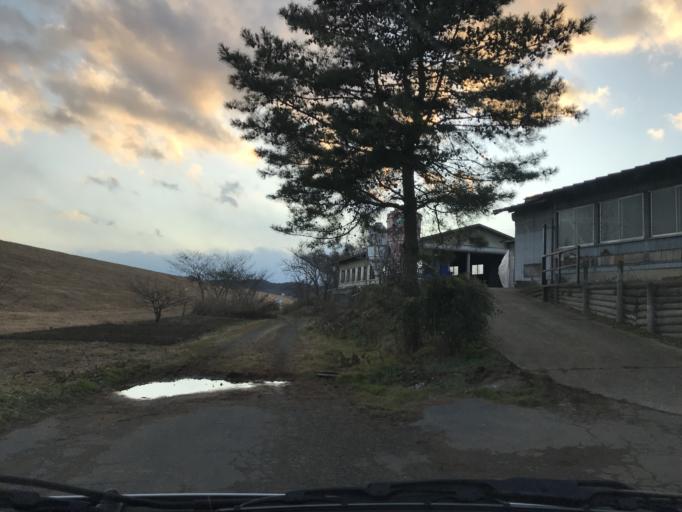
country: JP
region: Iwate
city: Ichinoseki
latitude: 39.0197
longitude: 141.1289
